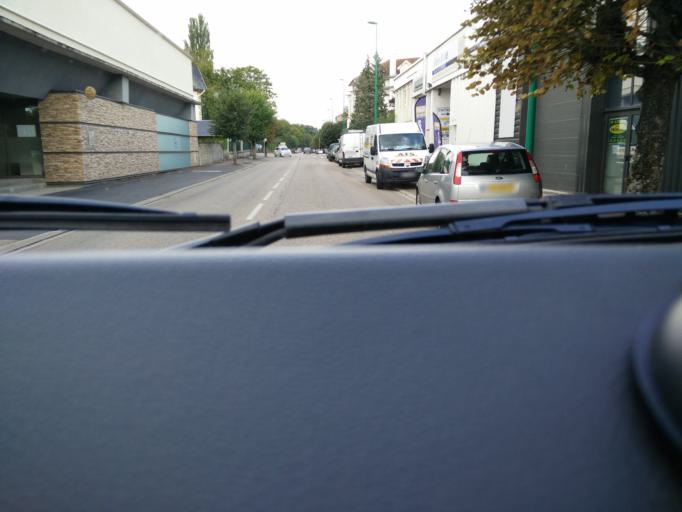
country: FR
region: Lorraine
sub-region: Departement de la Meuse
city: Verdun
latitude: 49.1619
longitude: 5.3919
